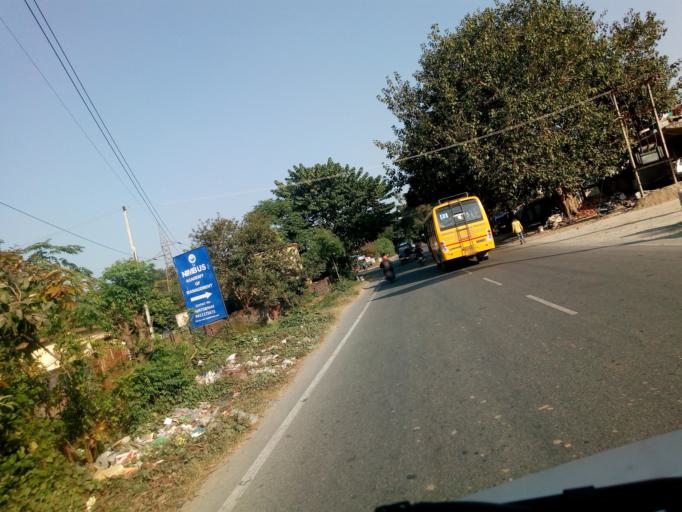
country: IN
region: Uttarakhand
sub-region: Dehradun
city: Dehradun
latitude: 30.3457
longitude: 77.9018
